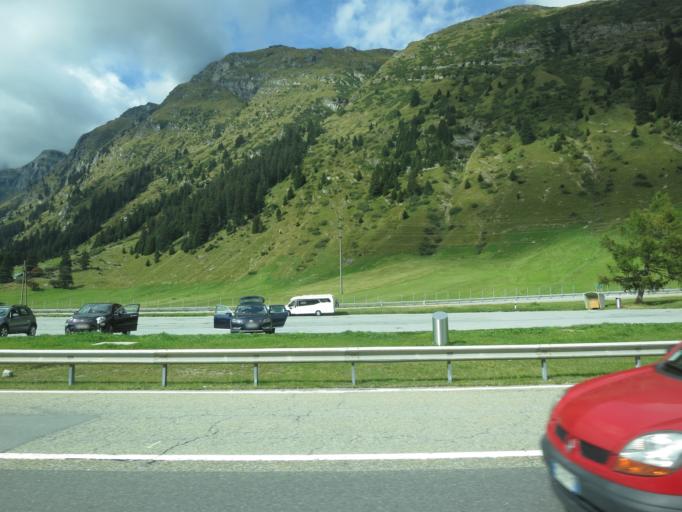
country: CH
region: Grisons
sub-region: Hinterrhein District
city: Hinterrhein
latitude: 46.5268
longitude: 9.1888
